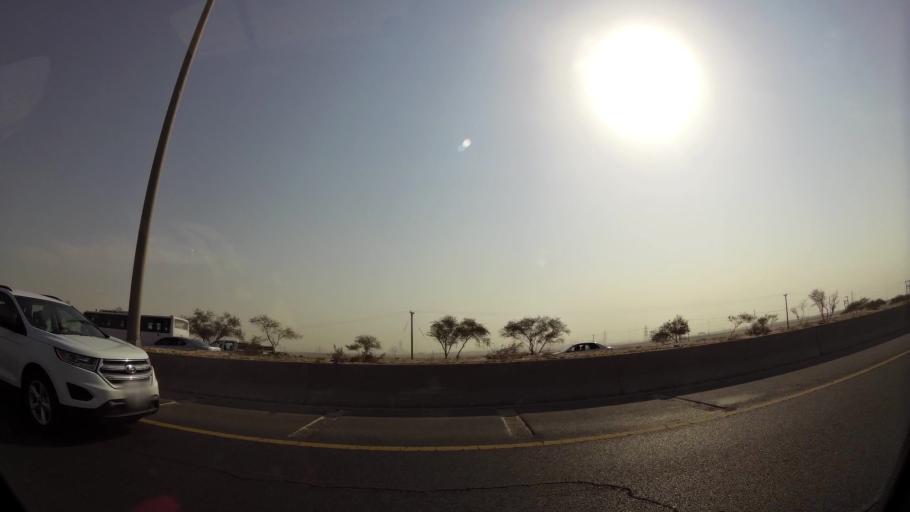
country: KW
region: Al Ahmadi
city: Al Ahmadi
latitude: 29.0414
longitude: 48.0937
